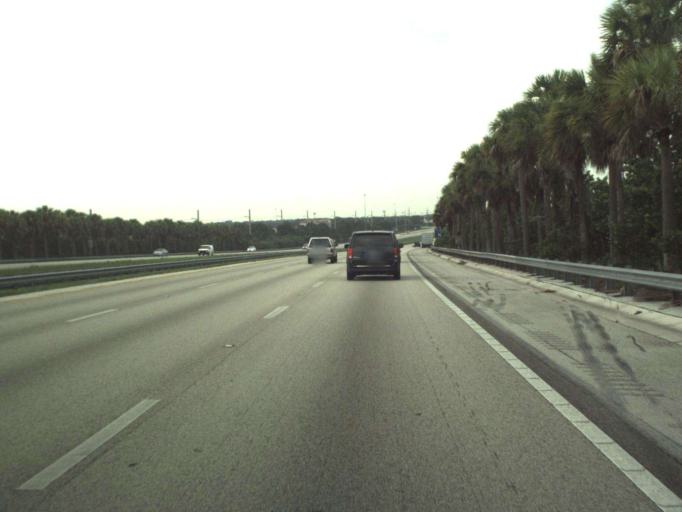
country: US
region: Florida
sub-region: Martin County
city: Palm City
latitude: 27.1179
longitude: -80.2679
